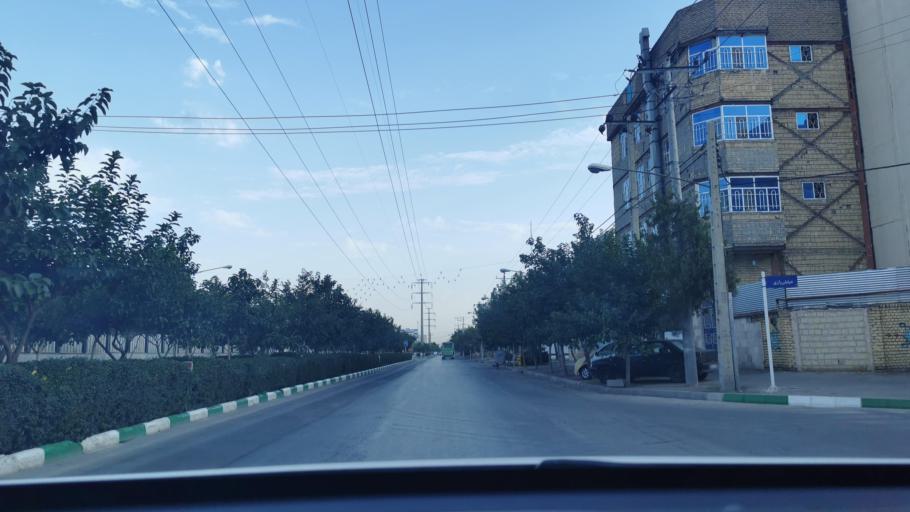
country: IR
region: Razavi Khorasan
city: Mashhad
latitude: 36.3523
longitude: 59.5293
